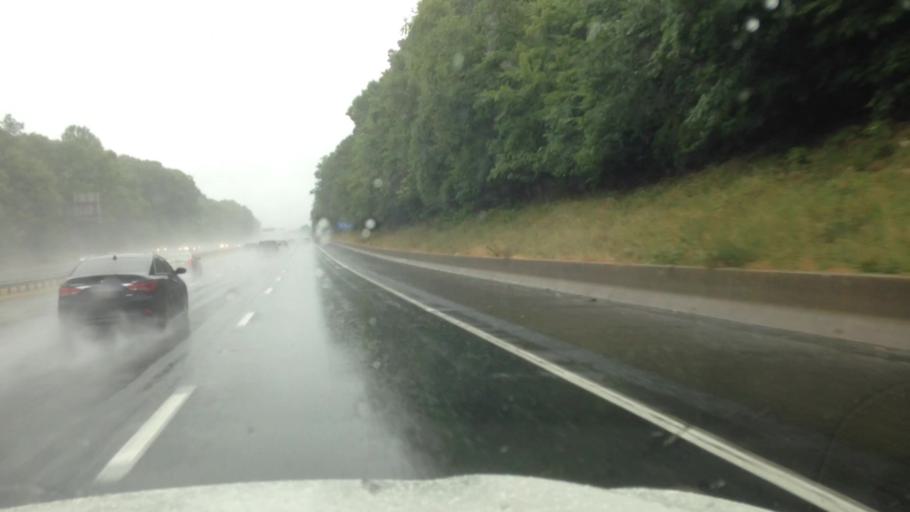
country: US
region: Maryland
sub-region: Prince George's County
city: Bowie
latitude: 38.9556
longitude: -76.6912
